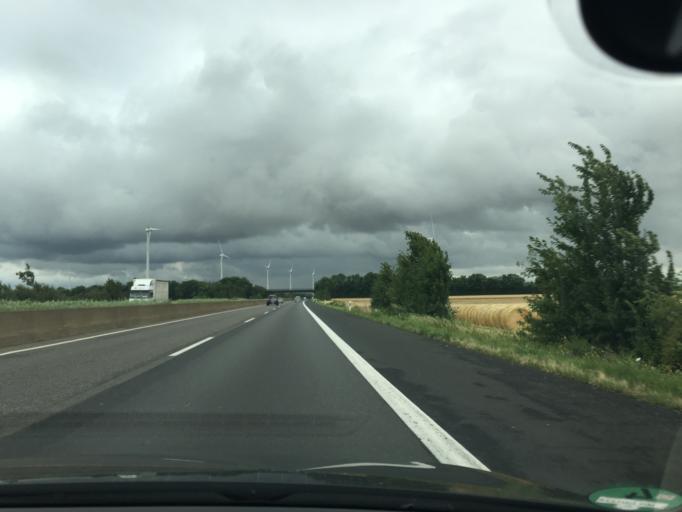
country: DE
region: North Rhine-Westphalia
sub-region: Regierungsbezirk Koln
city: Euskirchen
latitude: 50.7050
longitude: 6.7726
